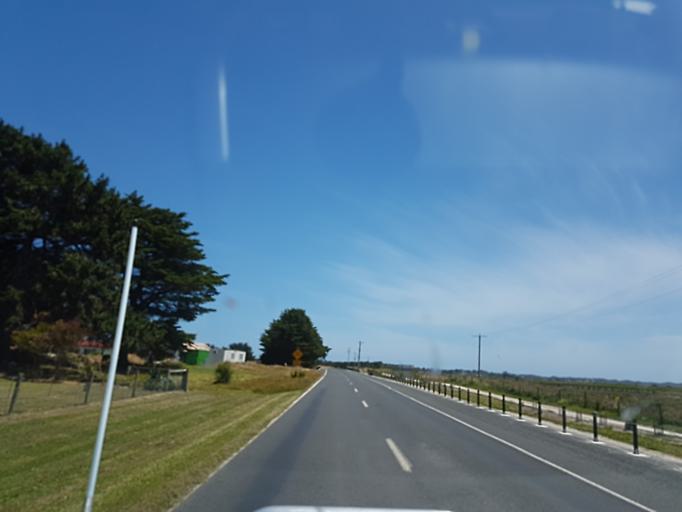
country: AU
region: Victoria
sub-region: Bass Coast
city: North Wonthaggi
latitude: -38.6968
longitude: 145.8622
